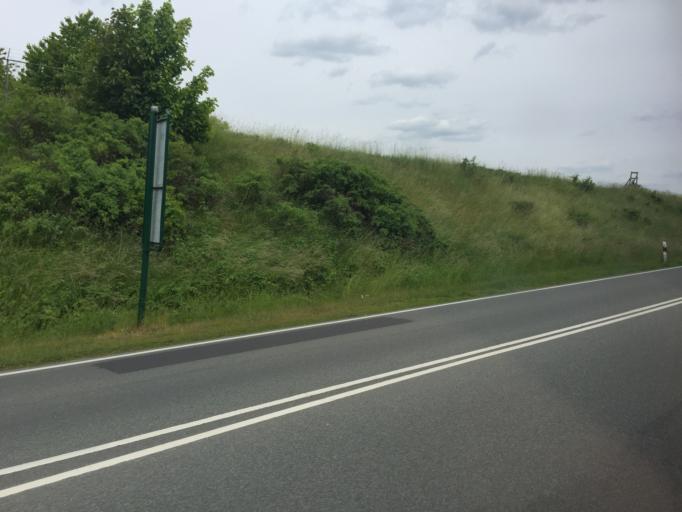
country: DE
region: Saxony
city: Markersdorf
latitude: 51.1486
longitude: 14.9178
